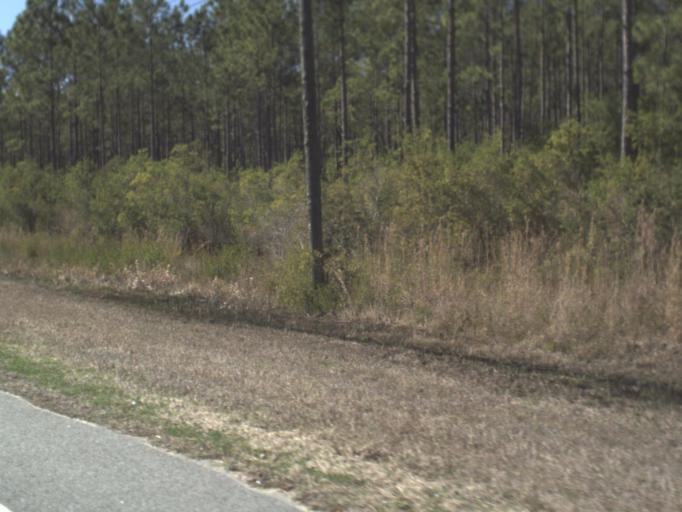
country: US
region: Florida
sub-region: Bay County
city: Laguna Beach
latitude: 30.3010
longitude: -85.8296
